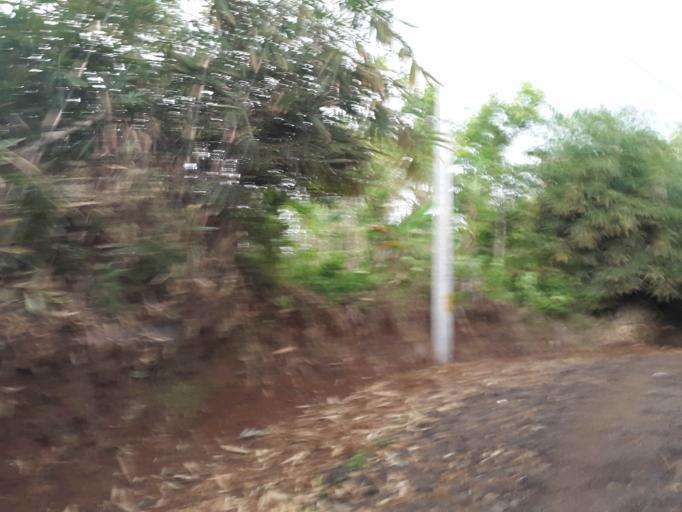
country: ID
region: Central Java
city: Limbangan
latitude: -7.2866
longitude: 108.7006
